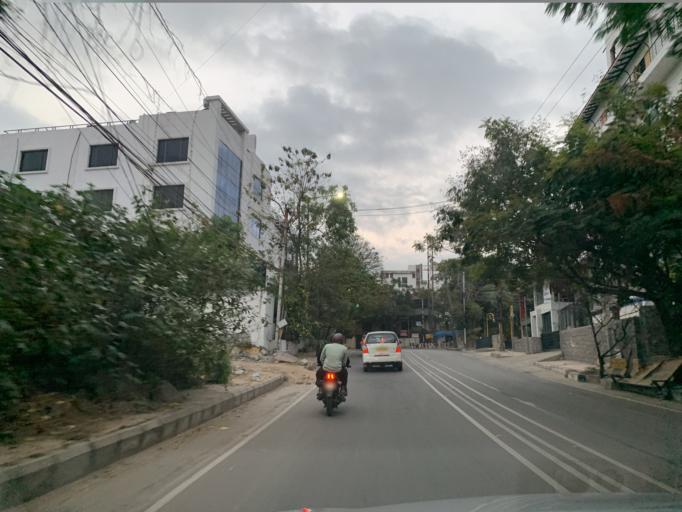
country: IN
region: Telangana
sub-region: Rangareddi
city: Kukatpalli
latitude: 17.4340
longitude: 78.3992
